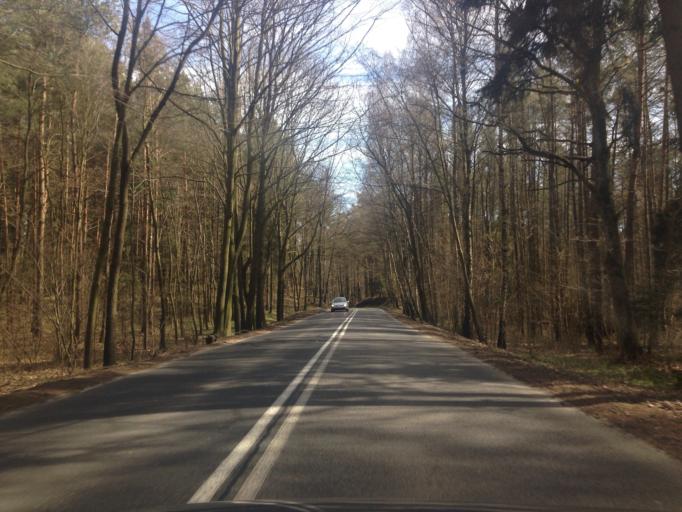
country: PL
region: Pomeranian Voivodeship
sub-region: Gdynia
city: Wielki Kack
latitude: 54.4800
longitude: 18.4477
